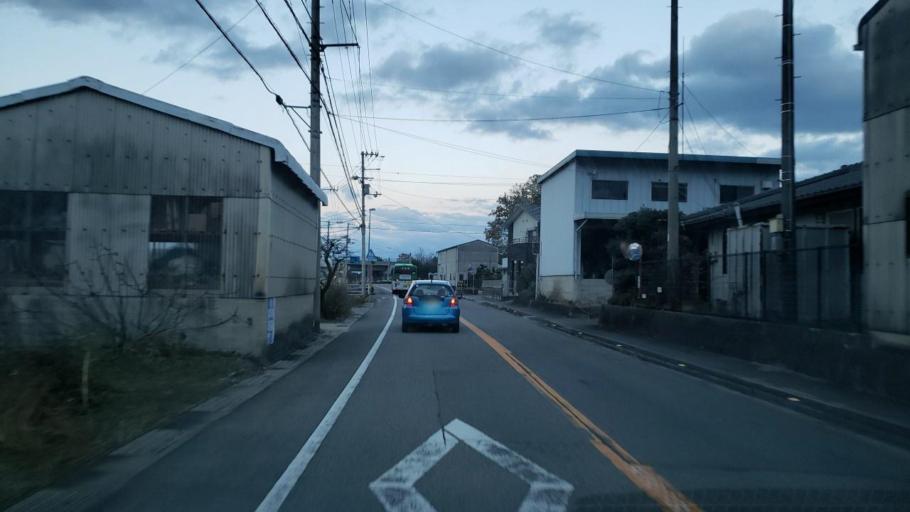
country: JP
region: Tokushima
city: Kamojimacho-jogejima
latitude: 34.2287
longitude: 134.3430
